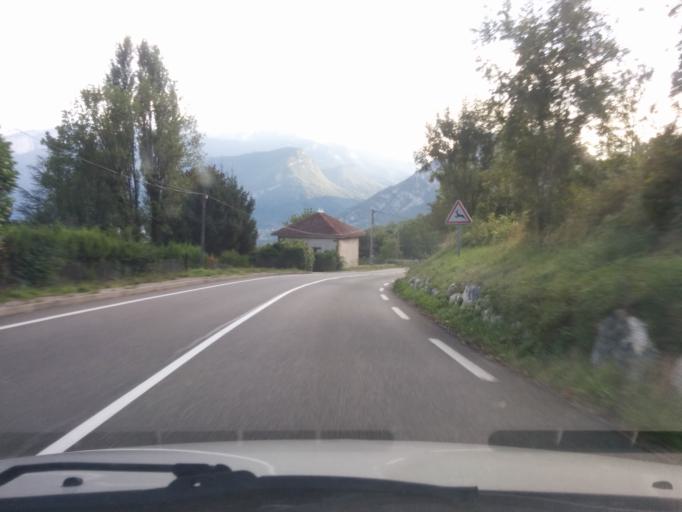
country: FR
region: Rhone-Alpes
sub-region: Departement de l'Isere
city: Voreppe
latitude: 45.3094
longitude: 5.6399
